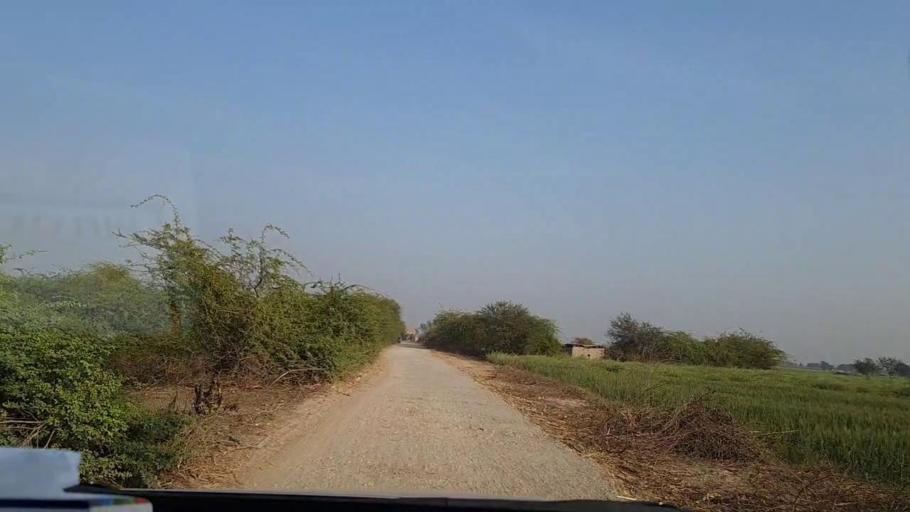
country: PK
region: Sindh
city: Tando Ghulam Ali
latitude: 25.2122
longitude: 68.8890
